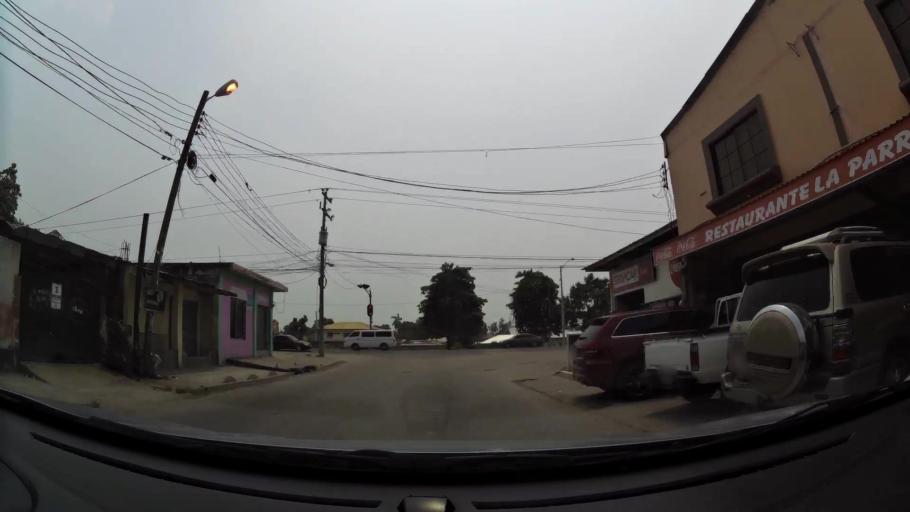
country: HN
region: Yoro
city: El Progreso
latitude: 15.3880
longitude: -87.8053
